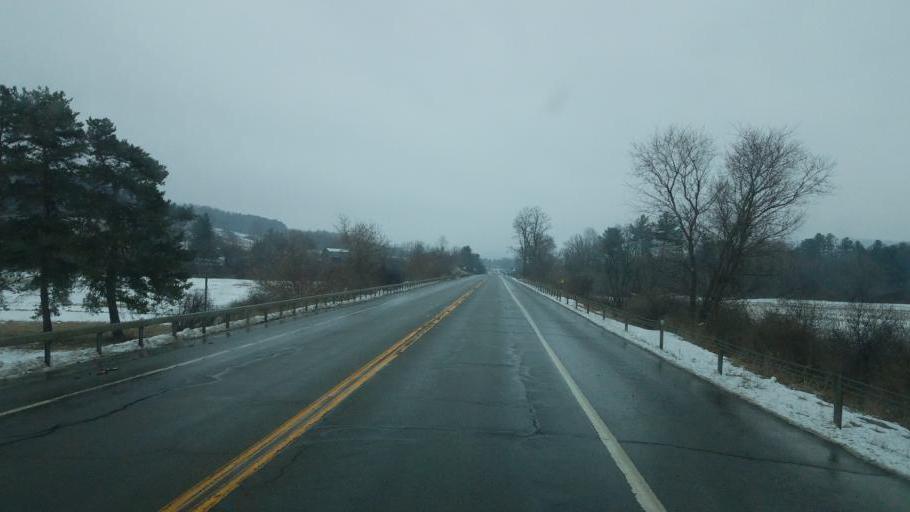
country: US
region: Pennsylvania
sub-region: Tioga County
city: Elkland
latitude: 42.0911
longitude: -77.4197
